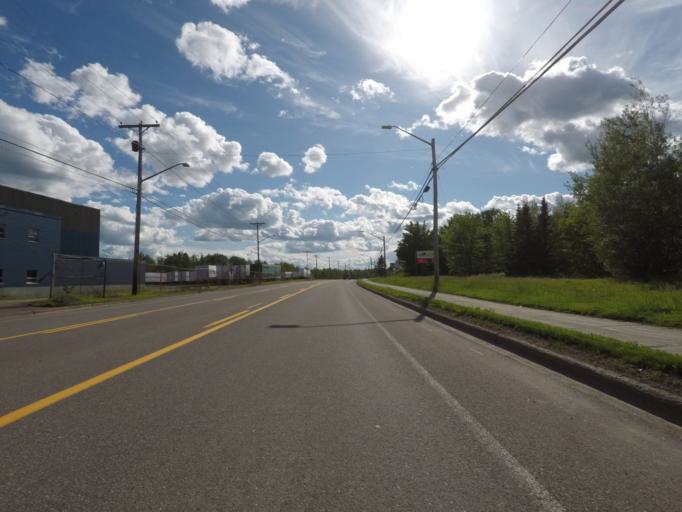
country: CA
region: New Brunswick
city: Moncton
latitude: 46.0949
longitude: -64.8267
